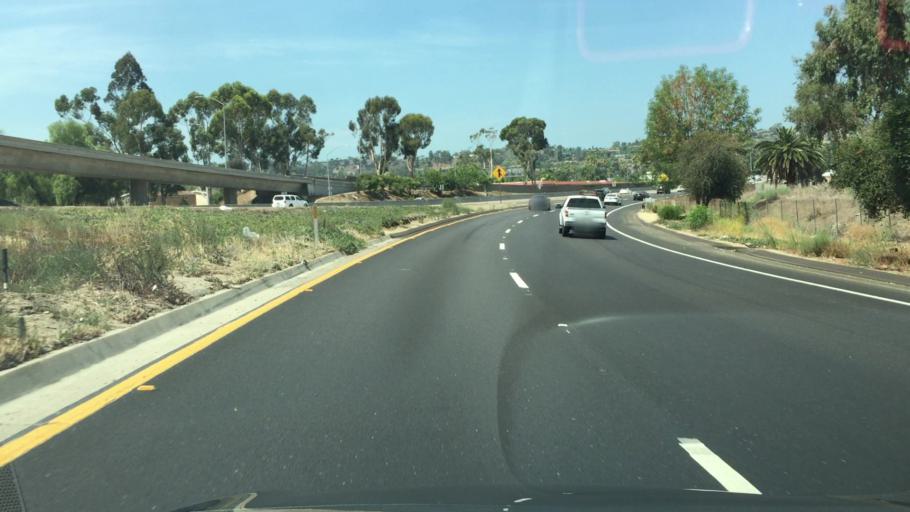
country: US
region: California
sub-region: San Diego County
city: El Cajon
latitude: 32.8037
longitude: -116.9642
